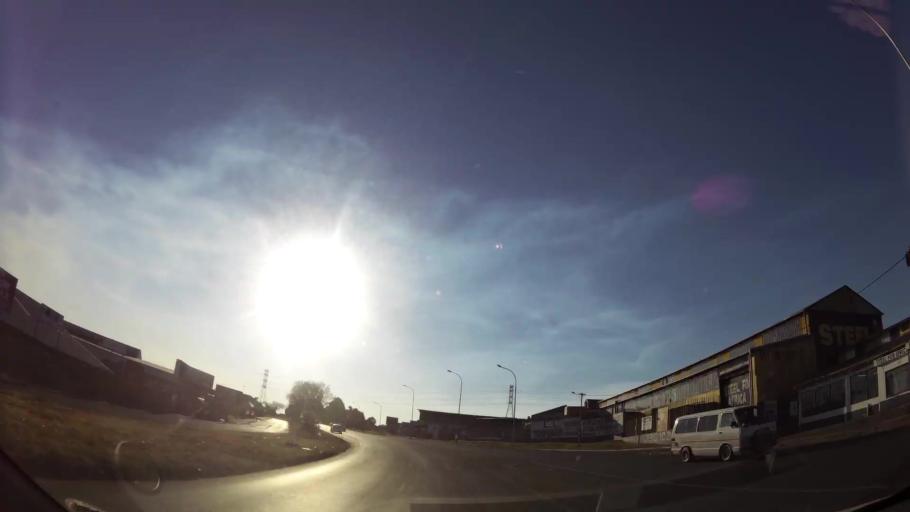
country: ZA
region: Gauteng
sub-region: City of Johannesburg Metropolitan Municipality
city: Roodepoort
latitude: -26.1441
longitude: 27.8612
